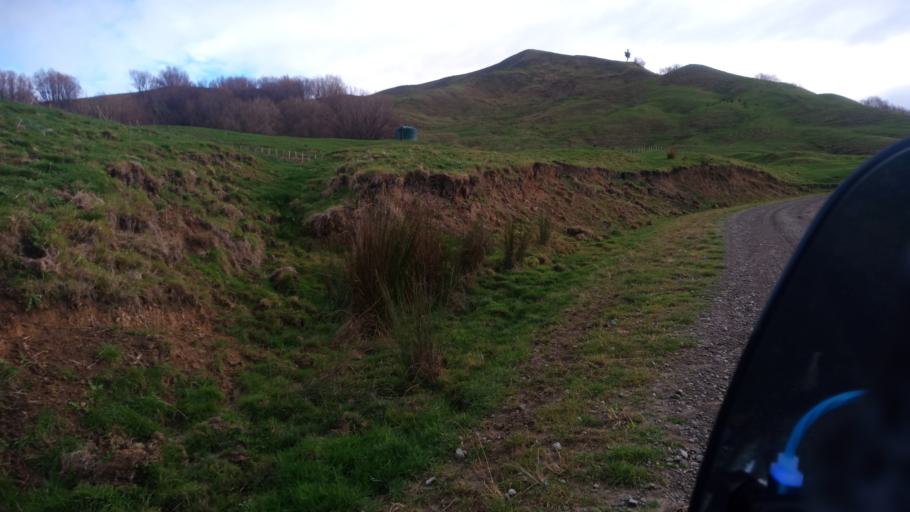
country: NZ
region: Gisborne
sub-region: Gisborne District
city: Gisborne
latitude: -38.3481
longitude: 177.9311
